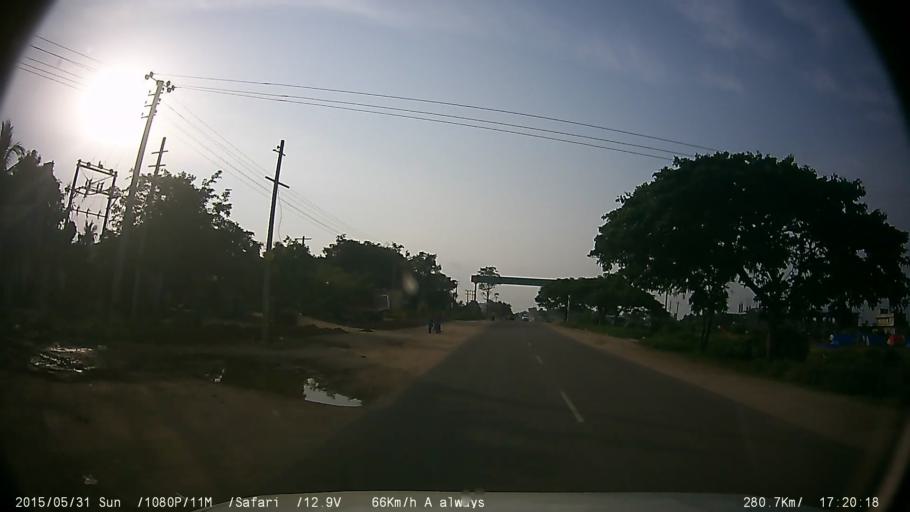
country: IN
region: Karnataka
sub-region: Chamrajnagar
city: Gundlupet
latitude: 11.8222
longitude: 76.6818
